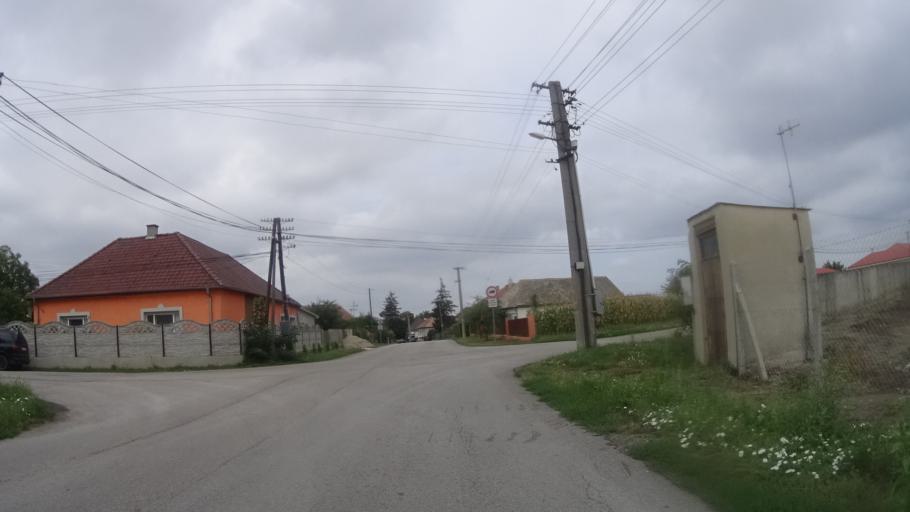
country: HU
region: Komarom-Esztergom
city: Acs
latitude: 47.7682
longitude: 17.9811
